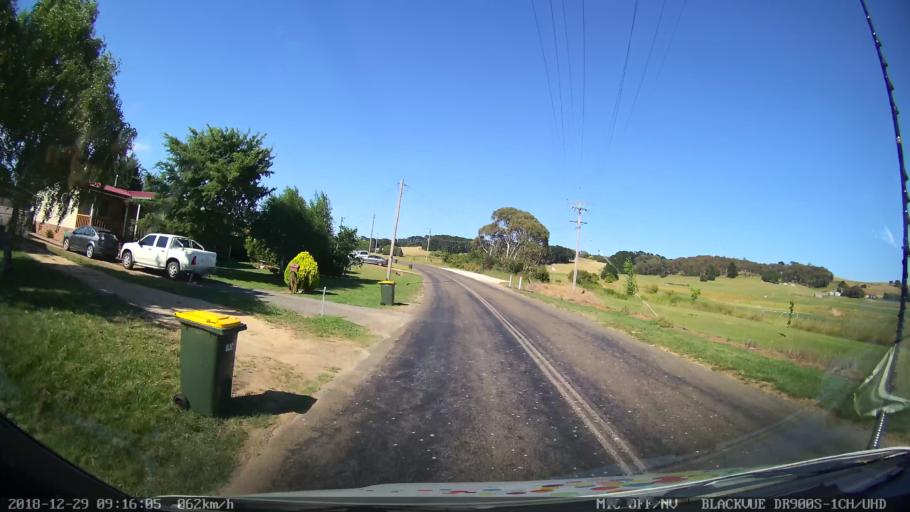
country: AU
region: New South Wales
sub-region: Upper Lachlan Shire
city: Crookwell
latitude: -34.4561
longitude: 149.4544
